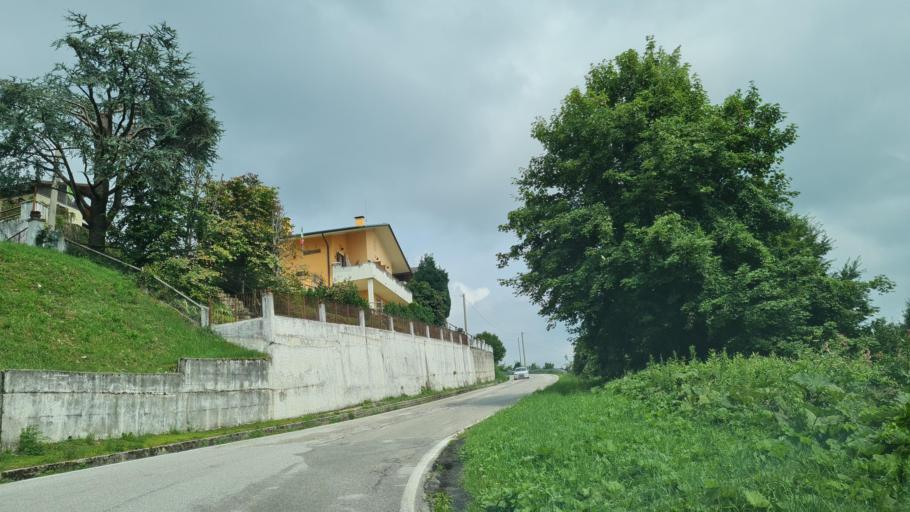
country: IT
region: Veneto
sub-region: Provincia di Vicenza
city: Conco
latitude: 45.8027
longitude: 11.6573
